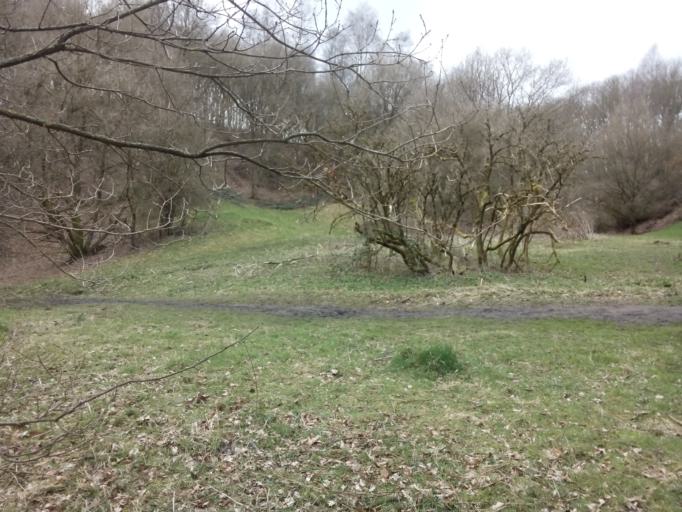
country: GB
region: England
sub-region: County Durham
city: Durham
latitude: 54.7801
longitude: -1.5923
